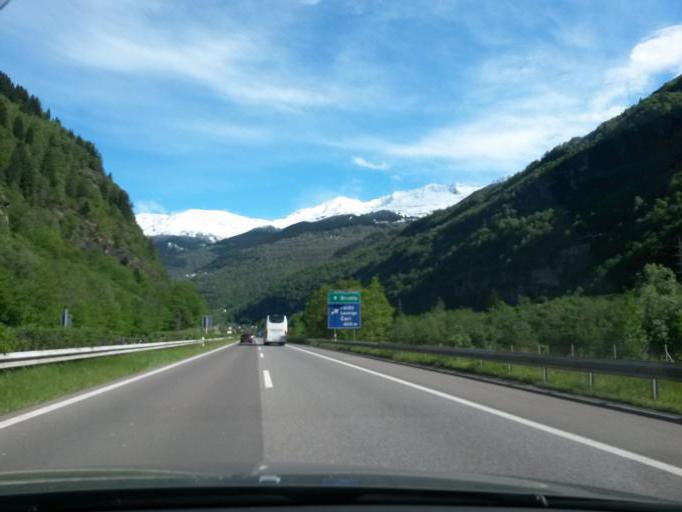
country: CH
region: Ticino
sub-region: Leventina District
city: Faido
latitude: 46.4544
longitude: 8.8272
